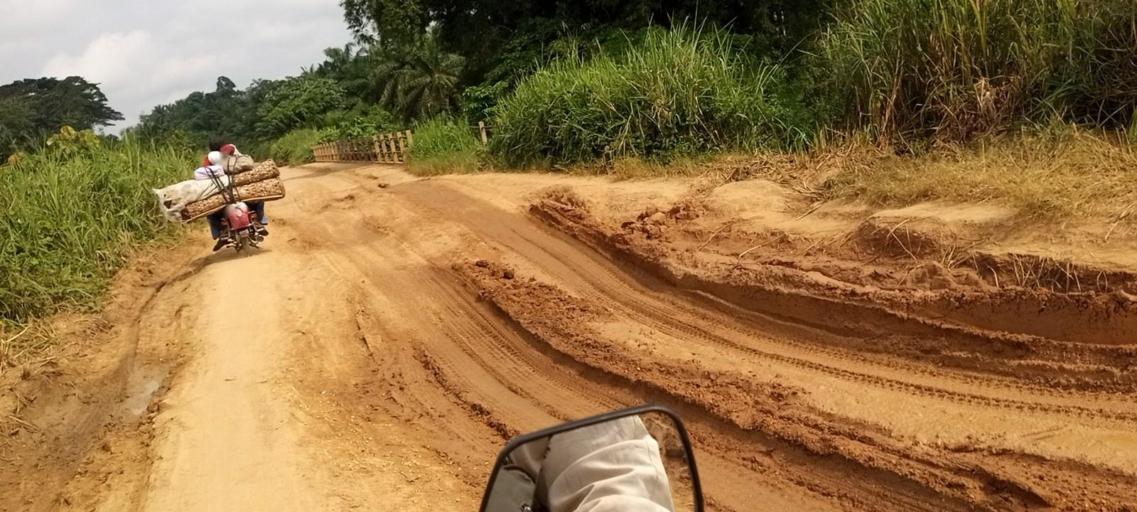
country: CD
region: Eastern Province
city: Kisangani
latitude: 0.3895
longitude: 25.3881
